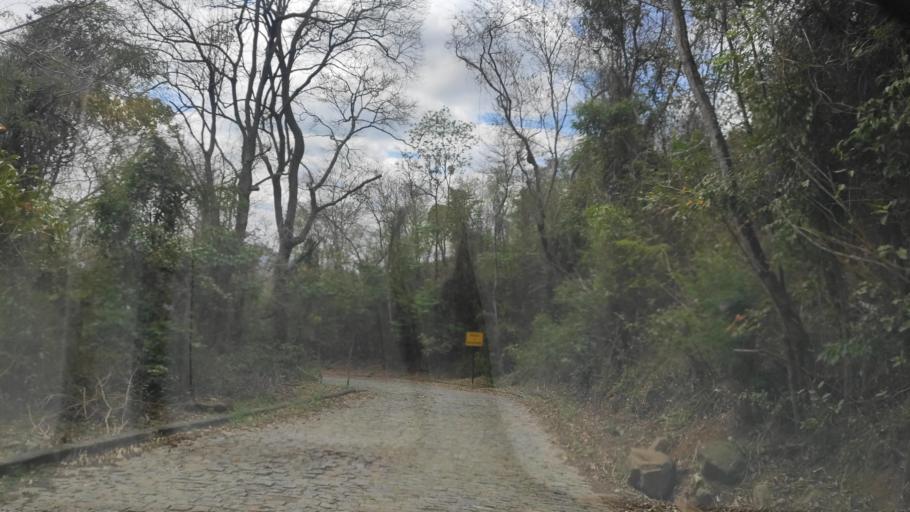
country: BR
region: Espirito Santo
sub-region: Vitoria
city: Vitoria
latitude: -20.2988
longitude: -40.3381
